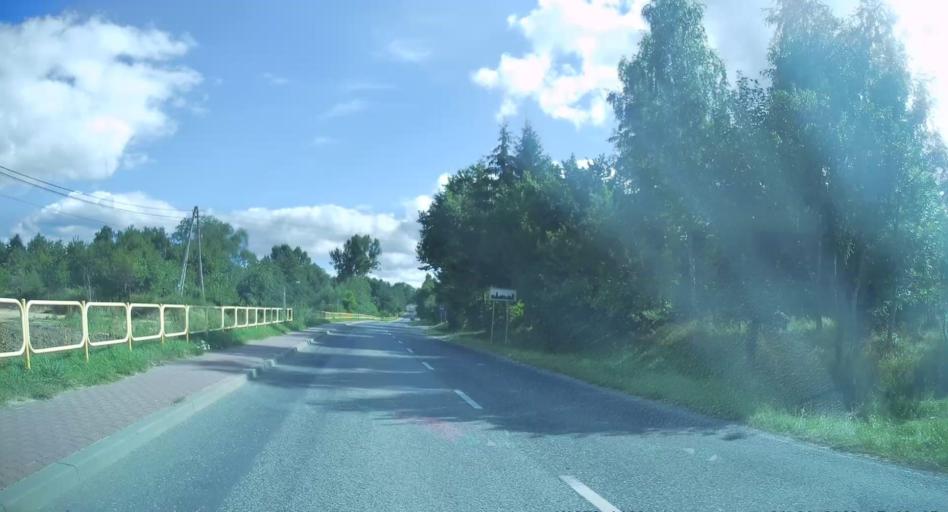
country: PL
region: Swietokrzyskie
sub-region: Powiat kielecki
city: Nowa Slupia
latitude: 50.8208
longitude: 21.0769
